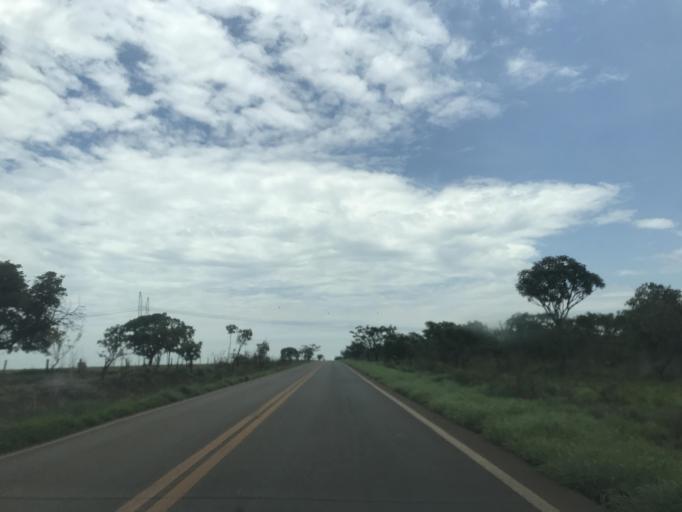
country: BR
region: Goias
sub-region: Luziania
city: Luziania
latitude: -16.2854
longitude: -48.0010
